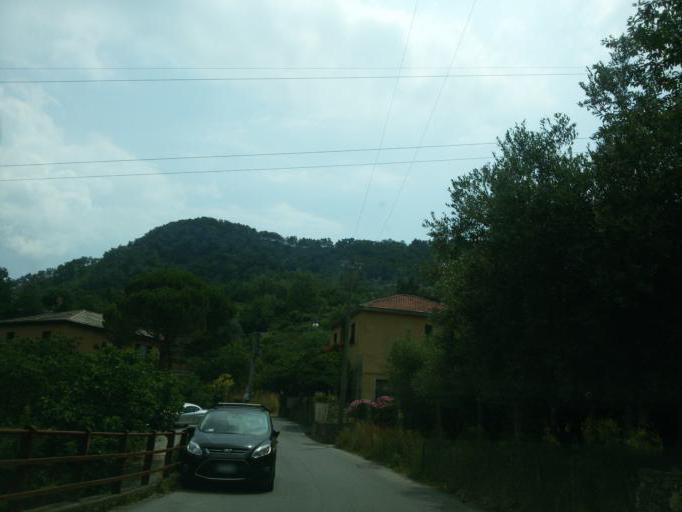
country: IT
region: Liguria
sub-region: Provincia di Genova
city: Piccarello
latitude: 44.4368
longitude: 9.0124
